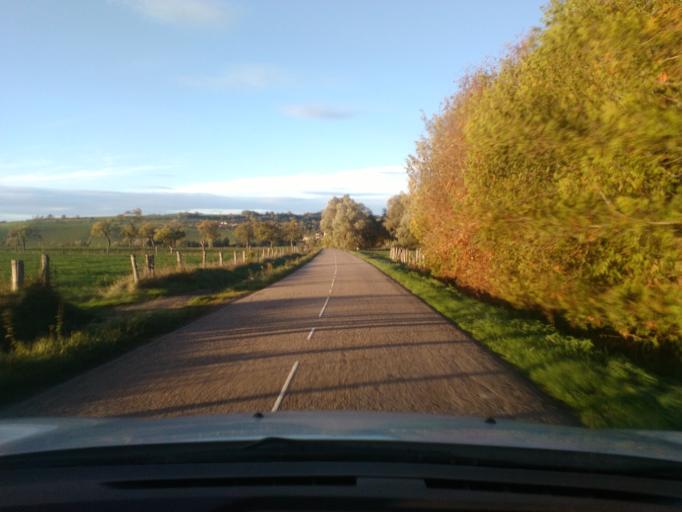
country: FR
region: Lorraine
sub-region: Departement des Vosges
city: Charmes
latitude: 48.3523
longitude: 6.2554
